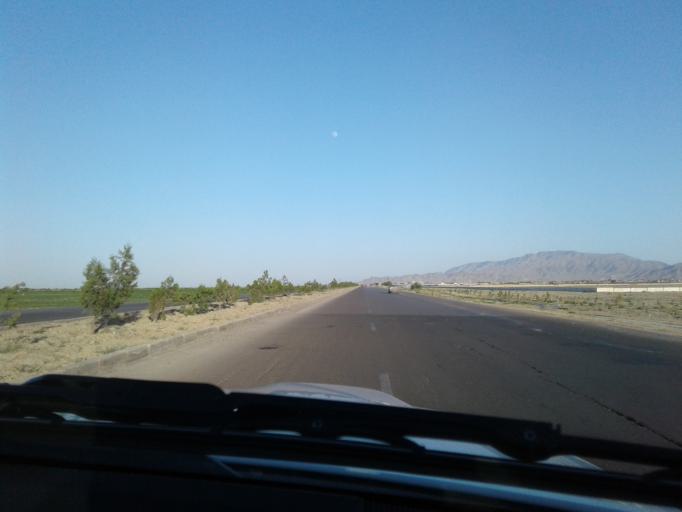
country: TM
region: Ahal
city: Baharly
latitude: 38.3353
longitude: 57.5724
